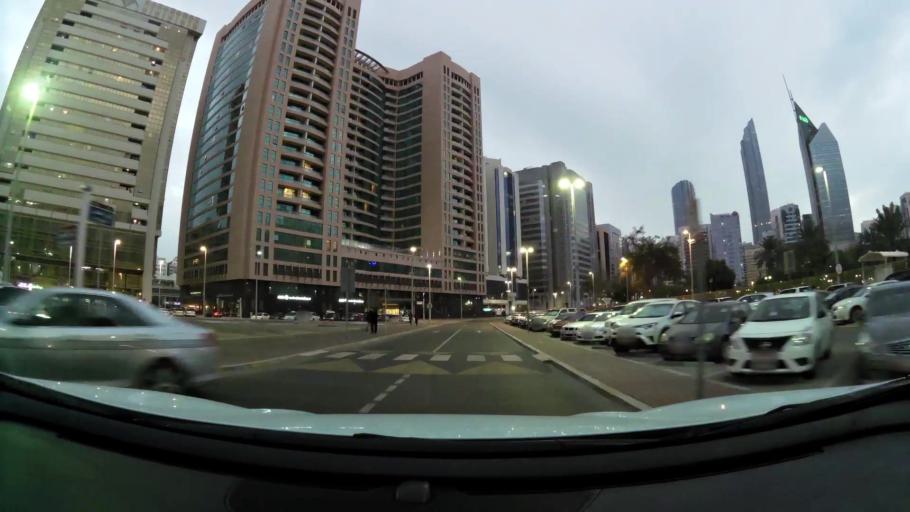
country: AE
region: Abu Dhabi
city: Abu Dhabi
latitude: 24.4930
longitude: 54.3652
